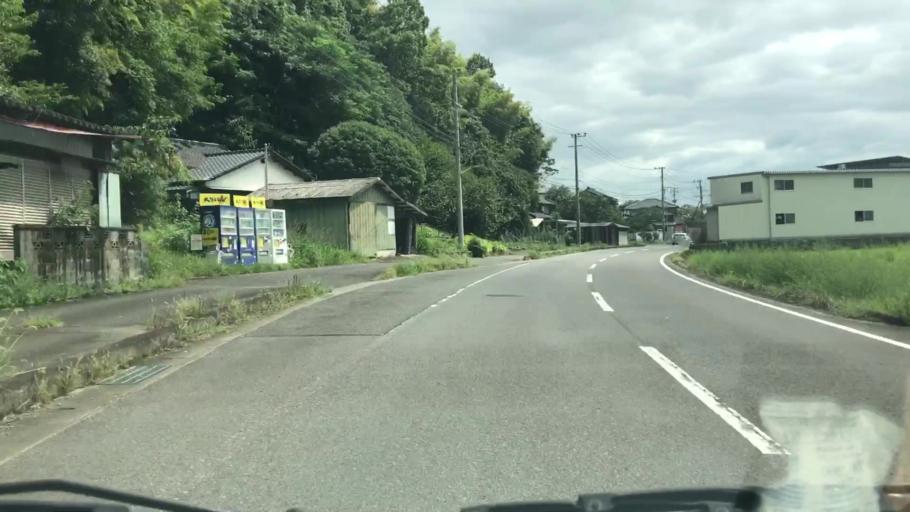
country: JP
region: Saga Prefecture
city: Takeocho-takeo
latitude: 33.2293
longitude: 130.1528
